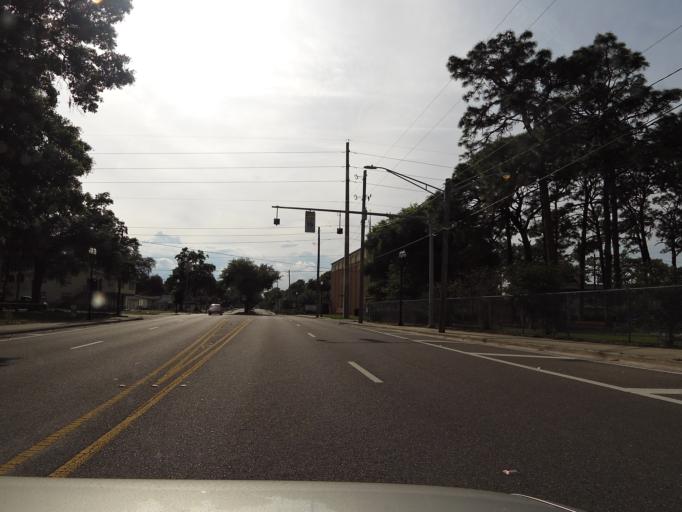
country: US
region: Florida
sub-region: Duval County
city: Jacksonville
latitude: 30.3336
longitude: -81.5908
